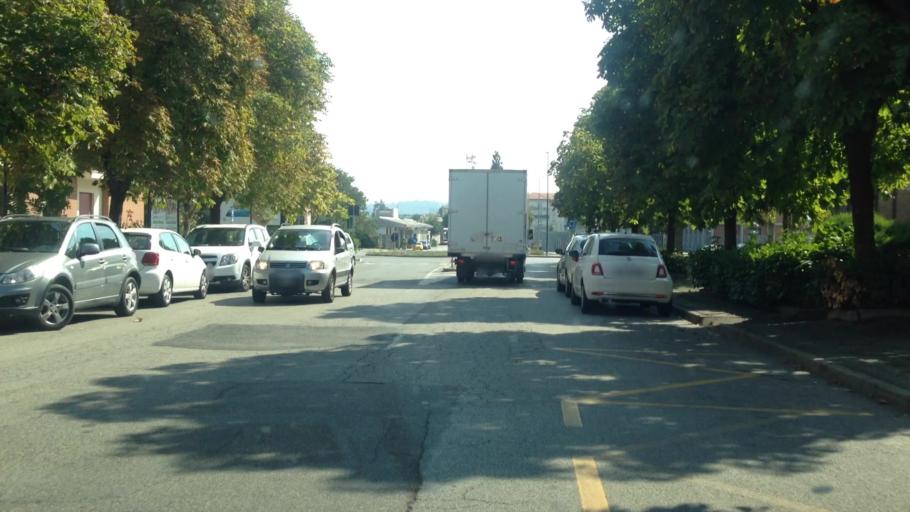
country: IT
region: Piedmont
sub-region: Provincia di Asti
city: Asti
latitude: 44.9053
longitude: 8.2248
